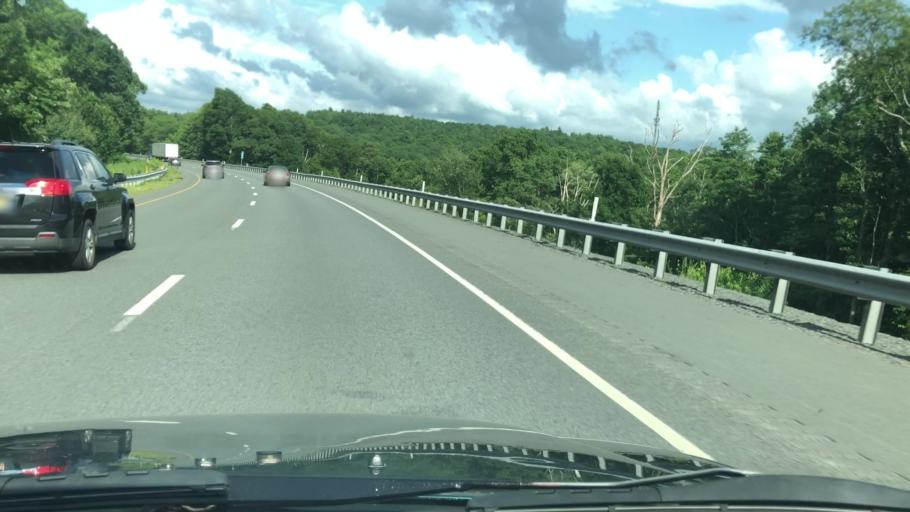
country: US
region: Pennsylvania
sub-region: Pike County
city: Milford
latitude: 41.3427
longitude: -74.8003
